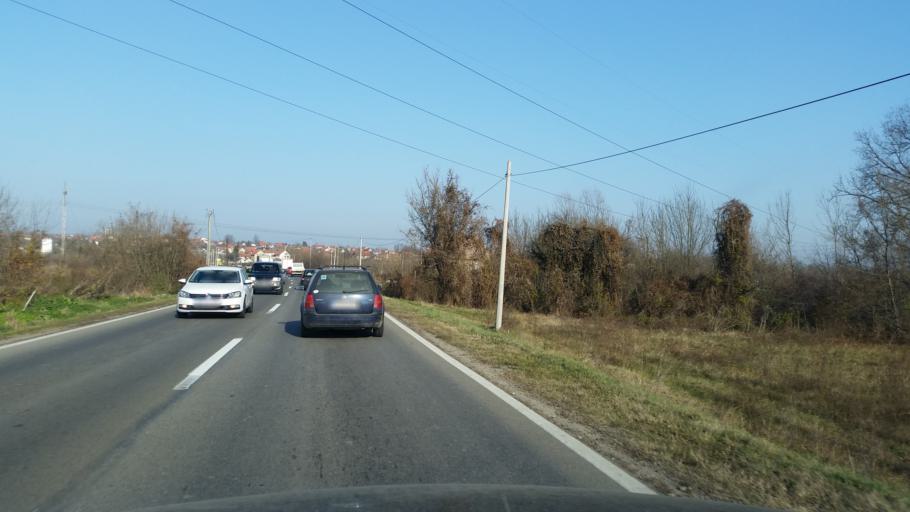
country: RS
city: Stepojevac
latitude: 44.4974
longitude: 20.2876
